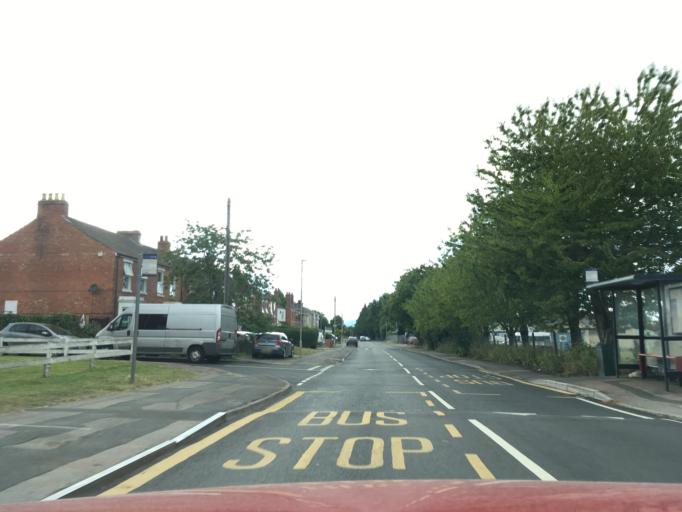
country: GB
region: England
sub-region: Gloucestershire
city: Gloucester
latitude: 51.8360
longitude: -2.2573
